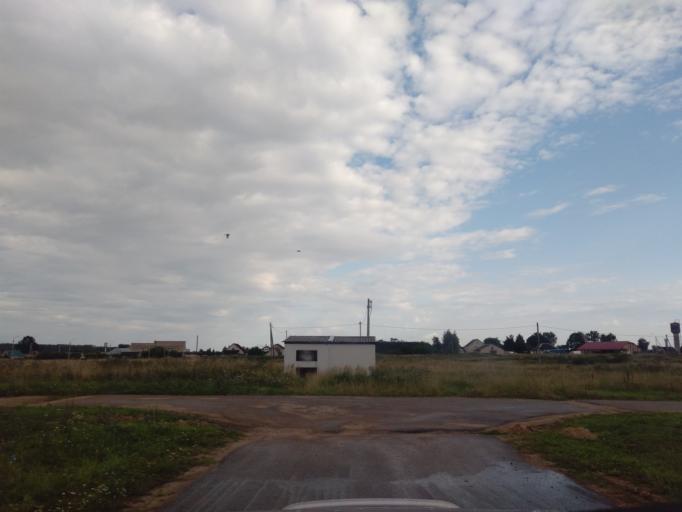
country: BY
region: Minsk
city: Kapyl'
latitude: 53.1634
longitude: 27.0785
